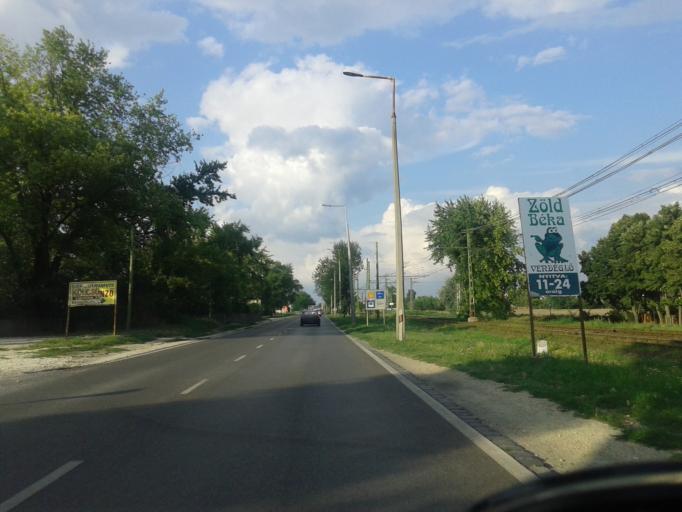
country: HU
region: Budapest
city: Budapest XXIII. keruelet
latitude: 47.3808
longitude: 19.1056
